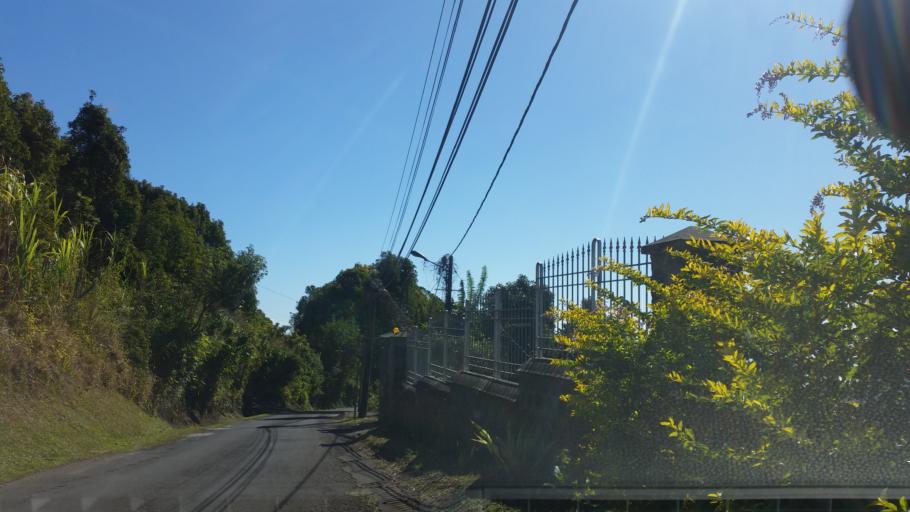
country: RE
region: Reunion
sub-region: Reunion
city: Sainte-Marie
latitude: -20.9434
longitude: 55.5295
